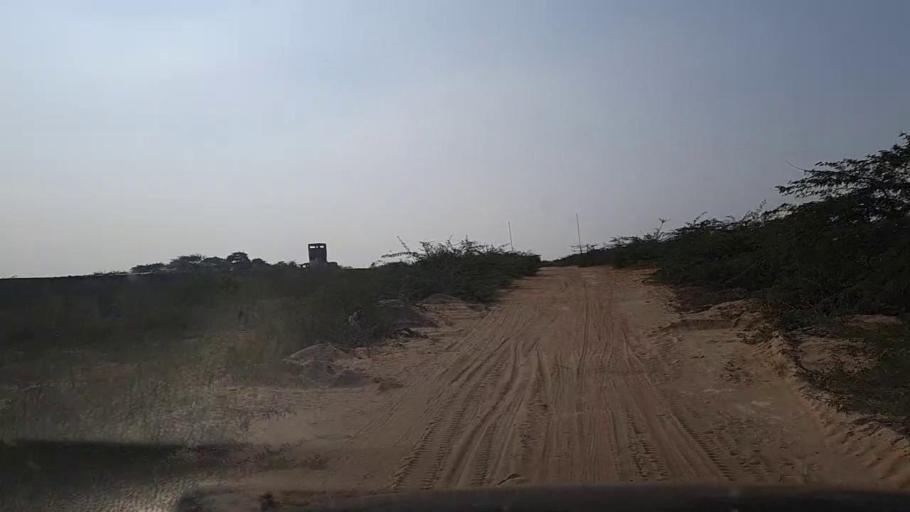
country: PK
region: Sindh
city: Gharo
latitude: 24.7490
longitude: 67.5679
